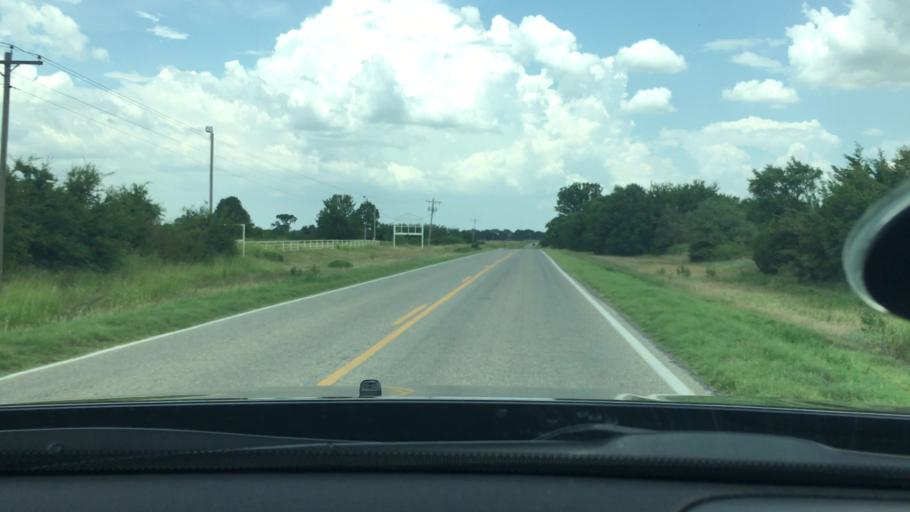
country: US
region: Oklahoma
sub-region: Marshall County
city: Oakland
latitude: 34.0126
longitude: -96.8788
